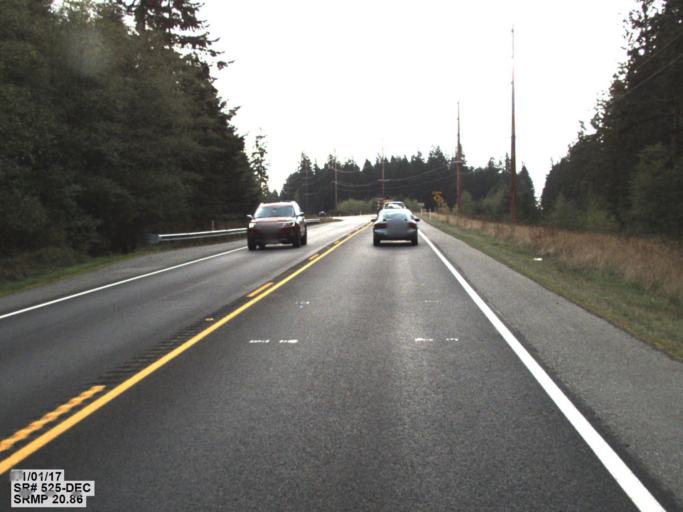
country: US
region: Washington
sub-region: Island County
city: Freeland
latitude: 48.0385
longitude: -122.5647
